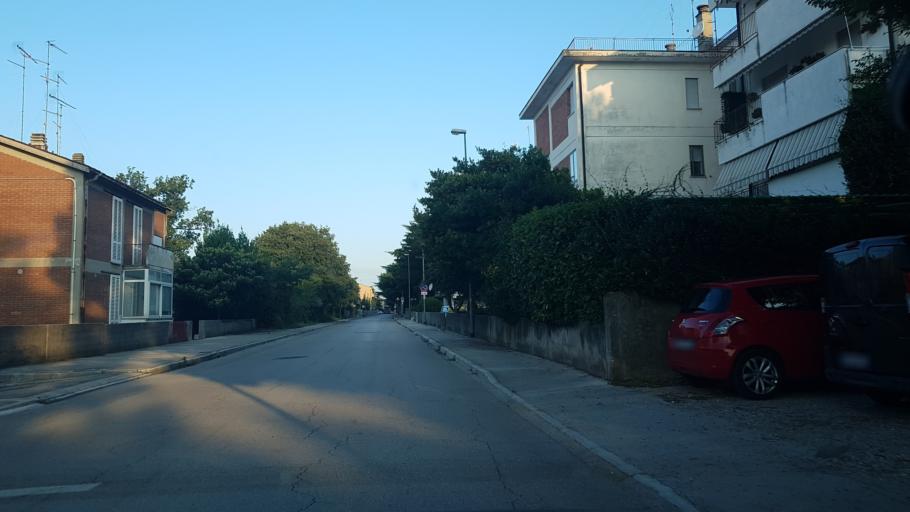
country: IT
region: Friuli Venezia Giulia
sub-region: Provincia di Gorizia
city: Monfalcone
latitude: 45.8026
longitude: 13.5564
